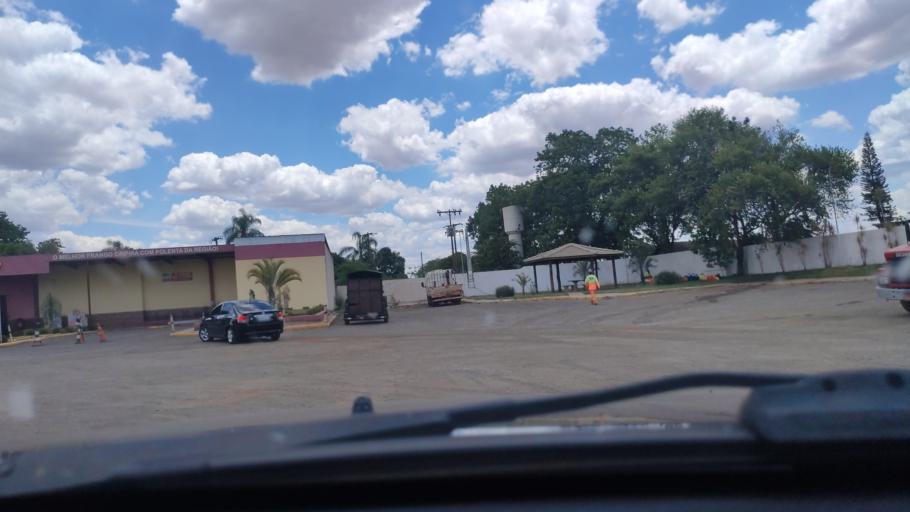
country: BR
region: Sao Paulo
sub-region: Santa Cruz Do Rio Pardo
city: Santa Cruz do Rio Pardo
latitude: -22.7653
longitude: -49.4948
